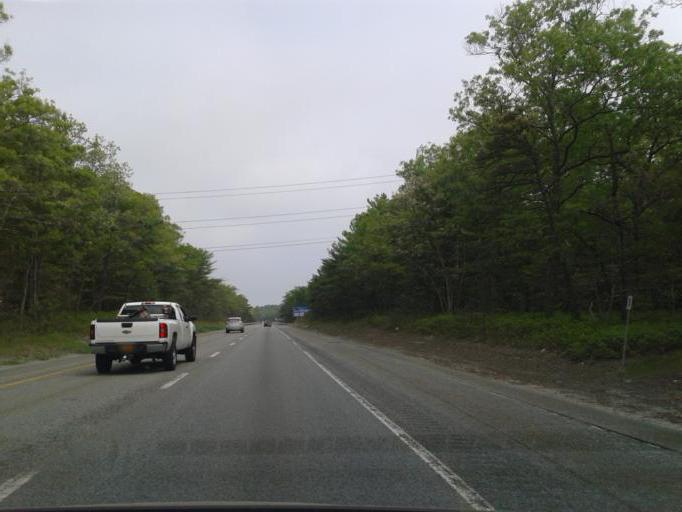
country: US
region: Massachusetts
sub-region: Plymouth County
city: Plymouth
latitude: 41.9069
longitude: -70.6177
